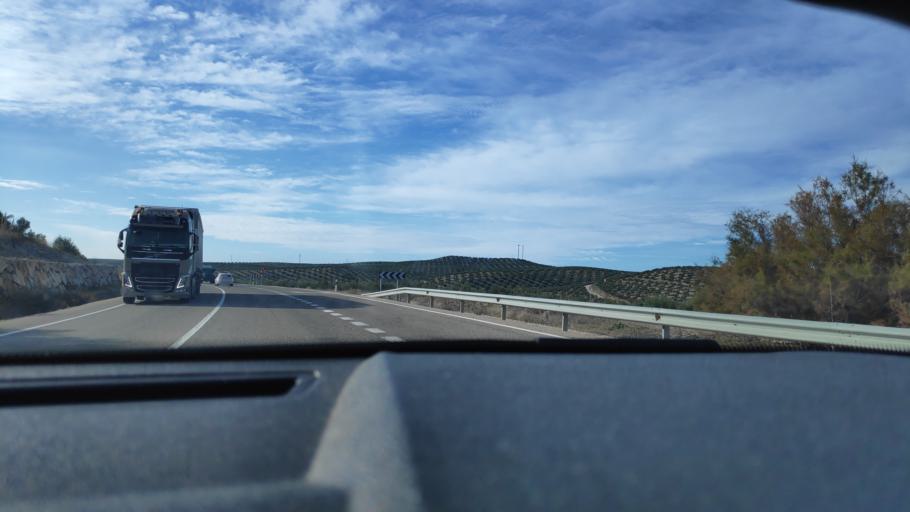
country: ES
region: Andalusia
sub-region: Provincia de Jaen
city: Porcuna
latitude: 37.8810
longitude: -4.2428
